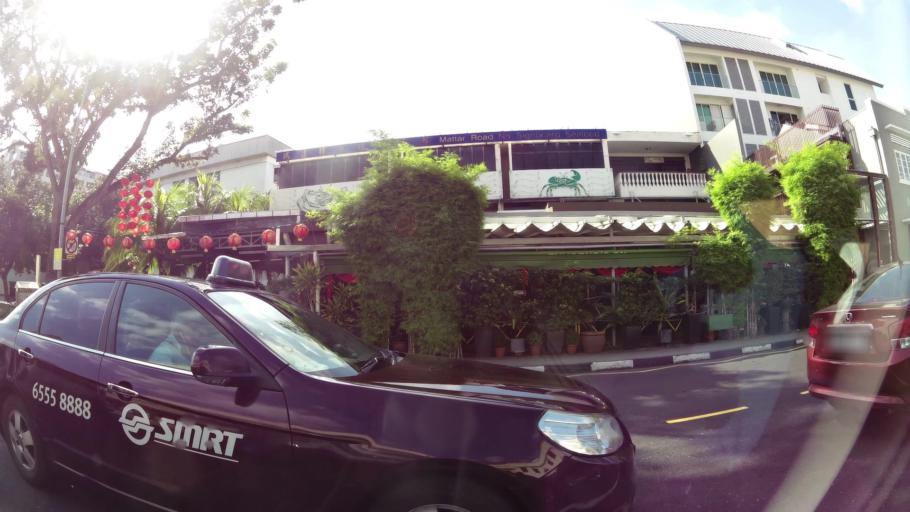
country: SG
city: Singapore
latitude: 1.3132
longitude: 103.8827
